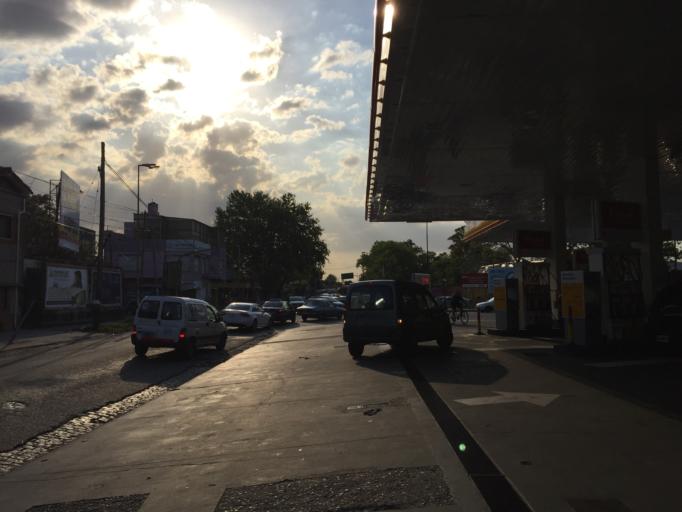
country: AR
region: Buenos Aires
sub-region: Partido de Lomas de Zamora
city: Lomas de Zamora
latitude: -34.7365
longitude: -58.3897
